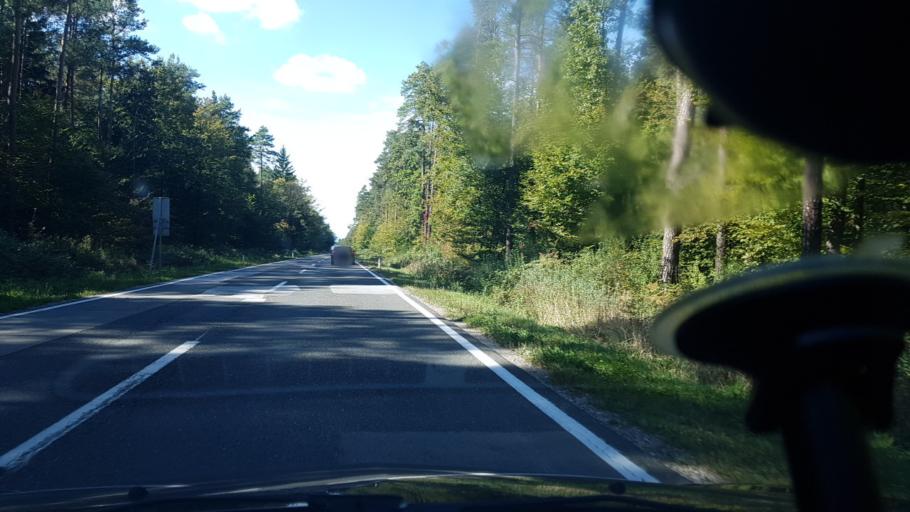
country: SI
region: Kidricevo
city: Kidricevo
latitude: 46.4109
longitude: 15.7804
